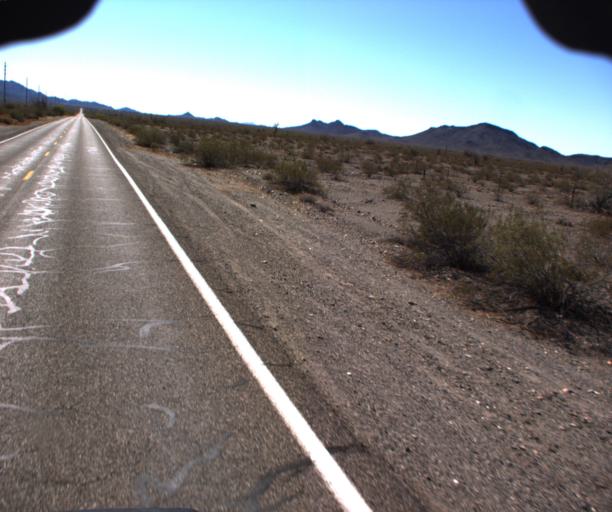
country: US
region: Arizona
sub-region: La Paz County
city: Salome
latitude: 33.7399
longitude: -113.7400
